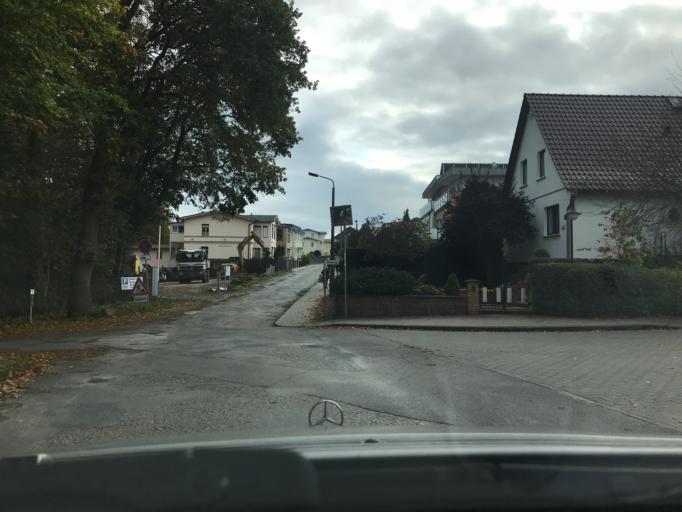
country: DE
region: Mecklenburg-Vorpommern
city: Seebad Heringsdorf
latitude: 53.9602
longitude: 14.1571
